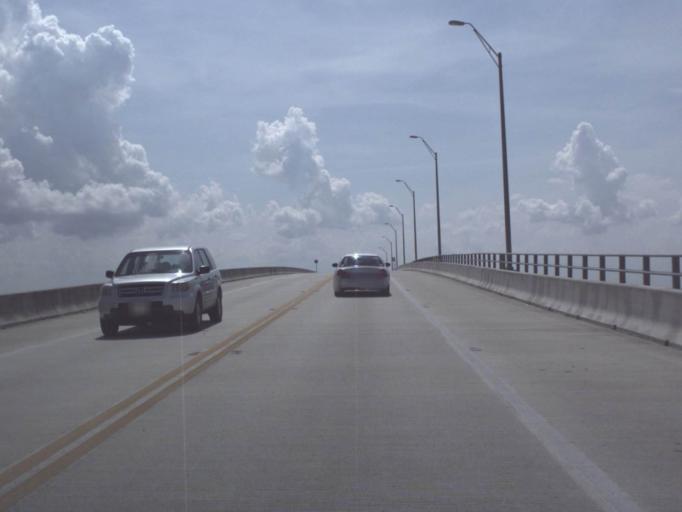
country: US
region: Florida
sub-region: Saint Johns County
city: Villano Beach
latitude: 29.9178
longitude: -81.2987
